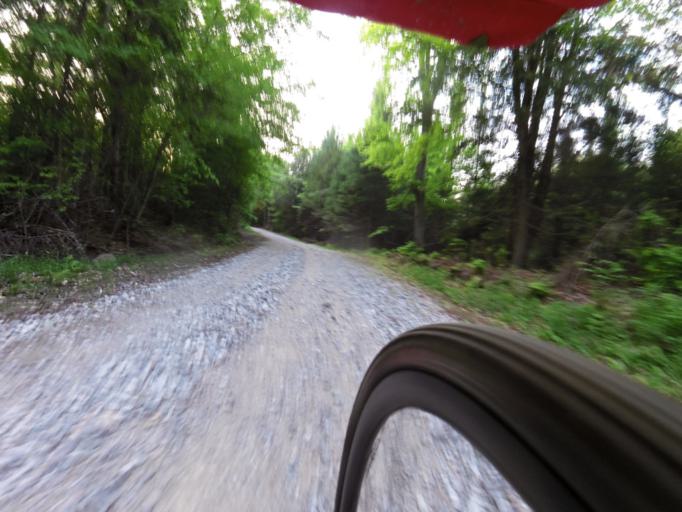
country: CA
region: Ontario
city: Arnprior
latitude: 45.1835
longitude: -76.5056
